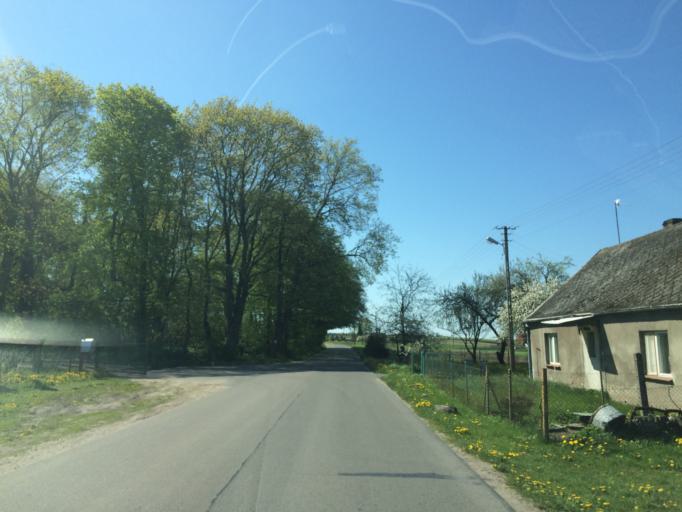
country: PL
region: Warmian-Masurian Voivodeship
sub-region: Powiat nowomiejski
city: Biskupiec
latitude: 53.5358
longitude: 19.4605
